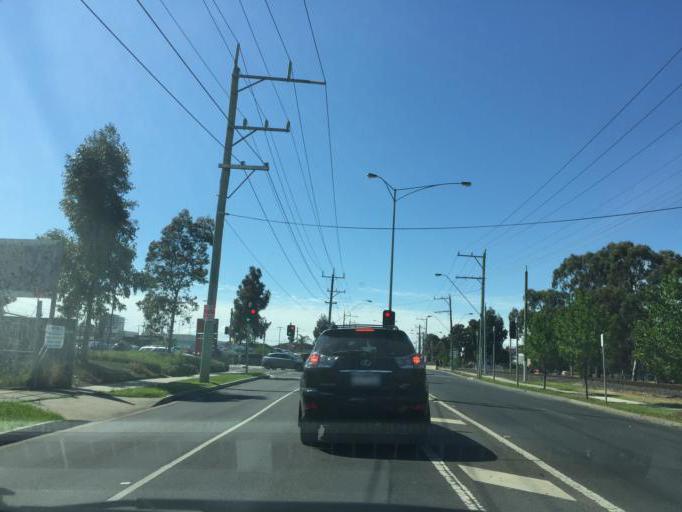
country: AU
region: Victoria
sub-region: Maribyrnong
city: Maribyrnong
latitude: -37.7773
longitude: 144.8851
